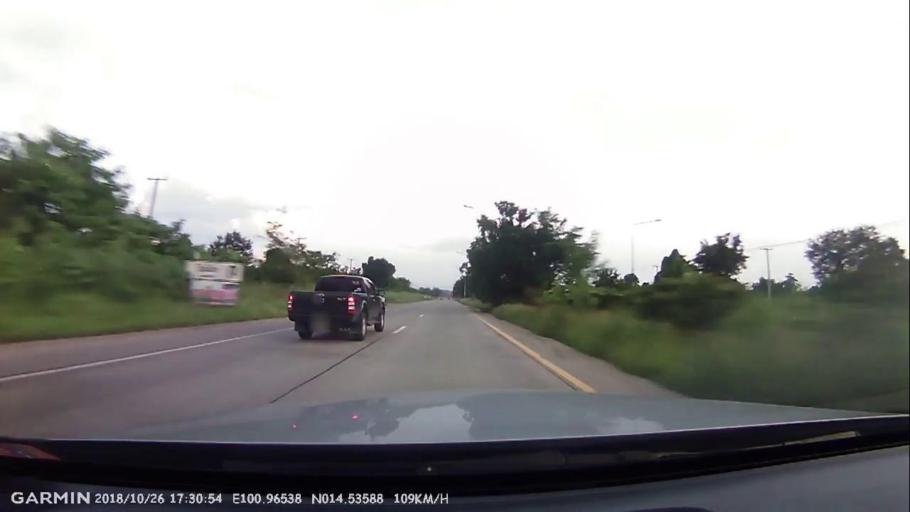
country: TH
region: Sara Buri
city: Saraburi
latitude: 14.5359
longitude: 100.9658
